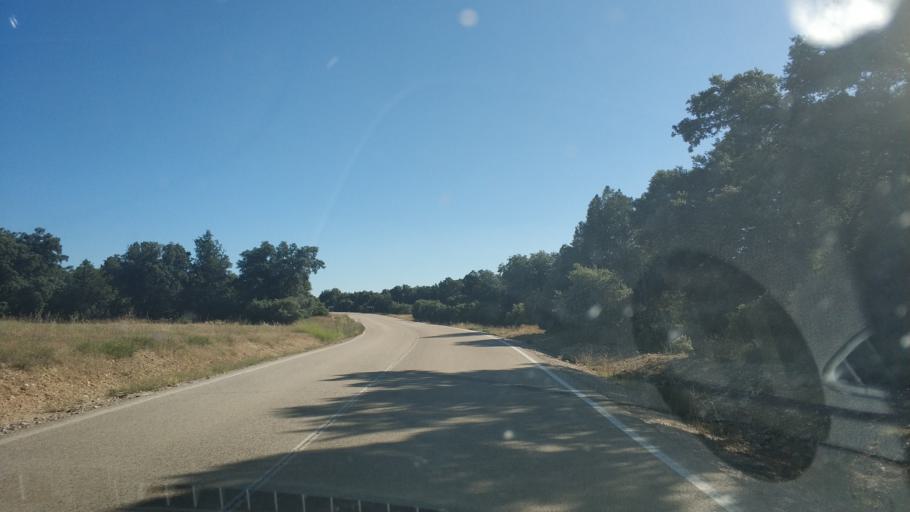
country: ES
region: Castille and Leon
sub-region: Provincia de Soria
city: Liceras
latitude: 41.4521
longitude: -3.2140
